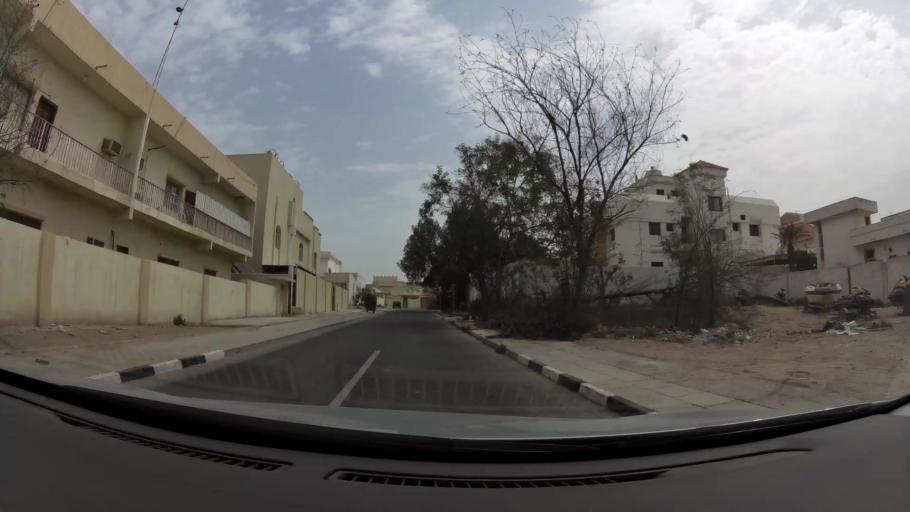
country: QA
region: Baladiyat ar Rayyan
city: Ar Rayyan
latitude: 25.3091
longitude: 51.4736
